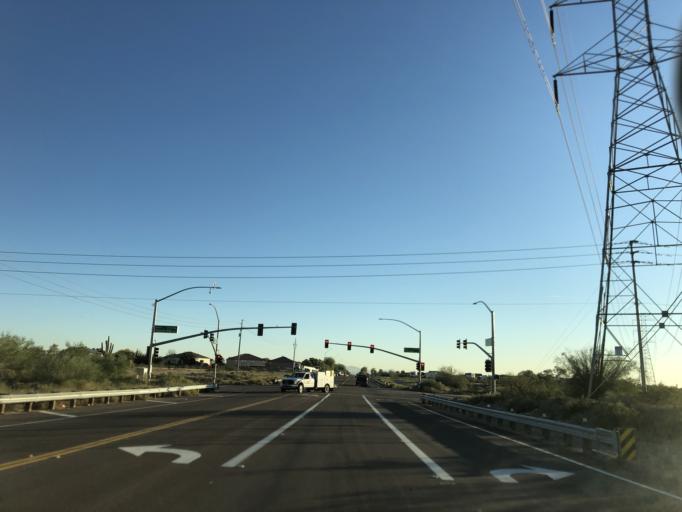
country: US
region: Arizona
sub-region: Maricopa County
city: Sun City West
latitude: 33.6969
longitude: -112.2897
